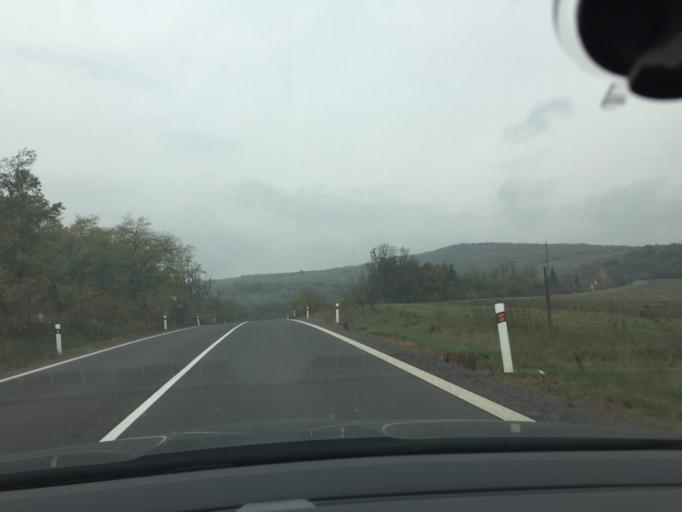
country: SK
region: Banskobystricky
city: Velky Krtis
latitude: 48.2241
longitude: 19.3793
